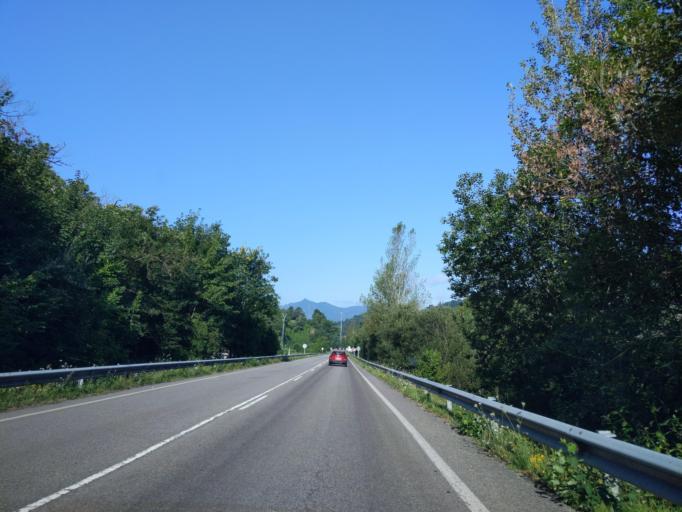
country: ES
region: Asturias
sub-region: Province of Asturias
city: Pola de Laviana
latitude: 43.2341
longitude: -5.4983
